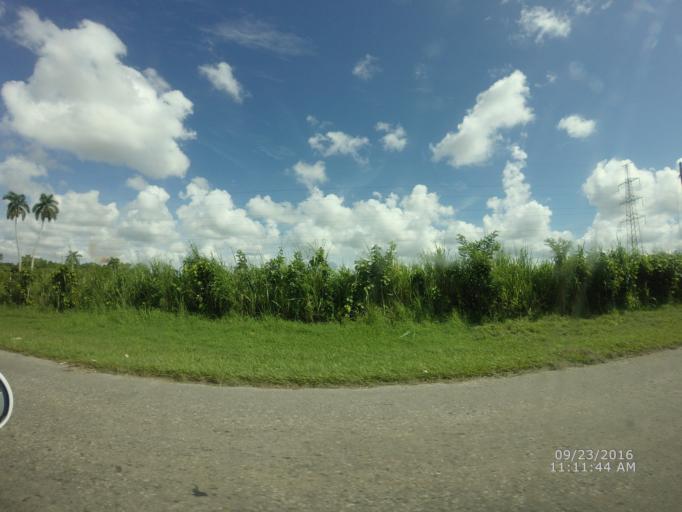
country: CU
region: La Habana
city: Arroyo Naranjo
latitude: 23.0265
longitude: -82.2734
